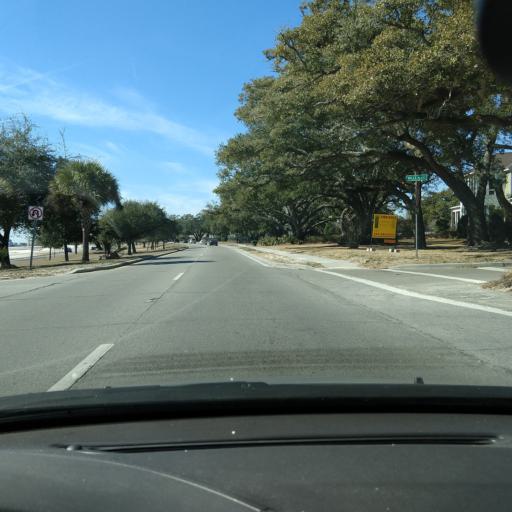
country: US
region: Mississippi
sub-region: Harrison County
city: Gulfport
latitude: 30.3717
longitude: -89.0741
